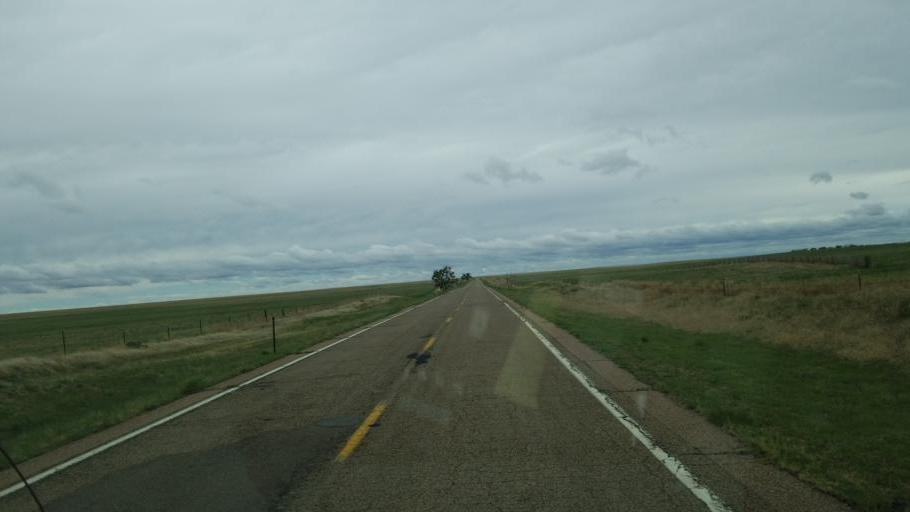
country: US
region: Colorado
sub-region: Lincoln County
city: Hugo
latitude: 38.8522
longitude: -103.7206
